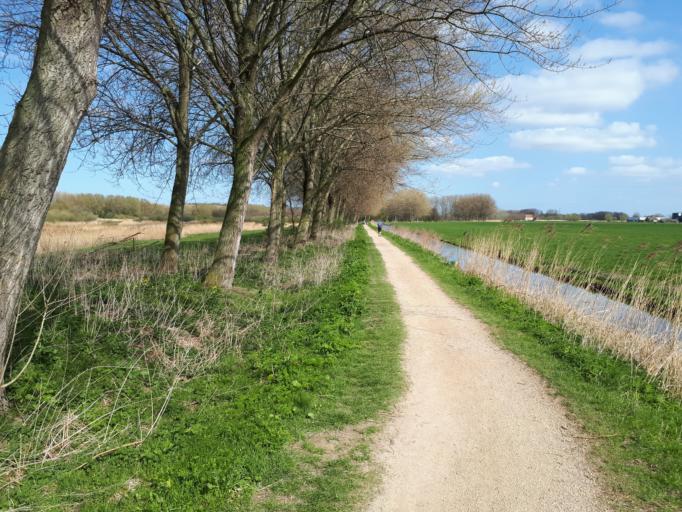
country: NL
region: South Holland
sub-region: Gemeente Pijnacker-Nootdorp
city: Pijnacker
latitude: 52.0206
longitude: 4.3975
